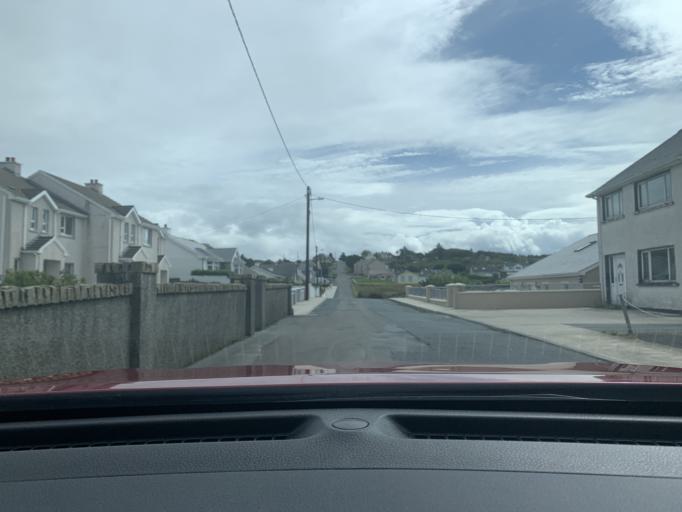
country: IE
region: Ulster
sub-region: County Donegal
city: Dungloe
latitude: 54.9475
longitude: -8.3594
